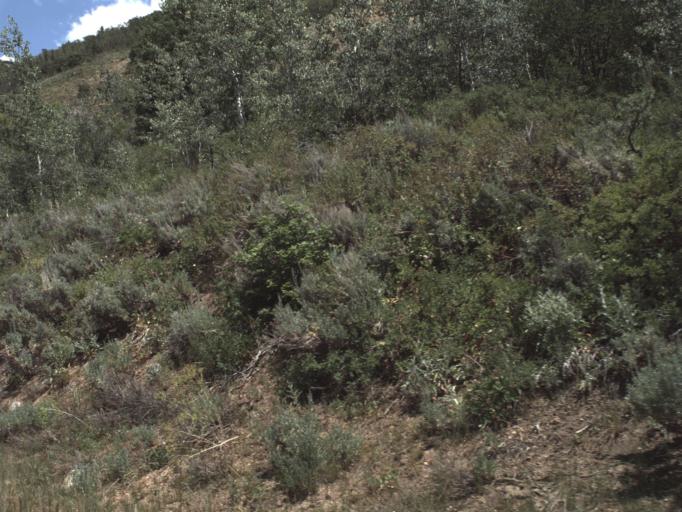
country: US
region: Utah
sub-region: Weber County
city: Wolf Creek
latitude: 41.3632
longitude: -111.5921
